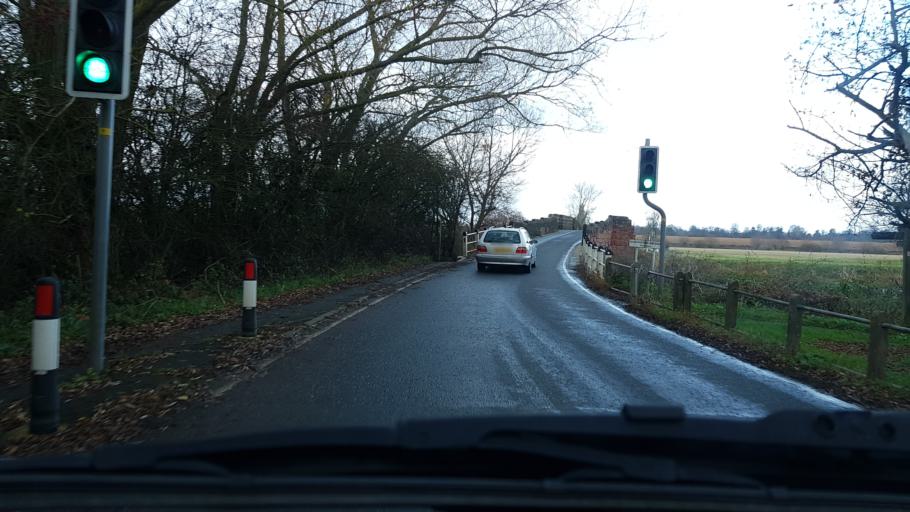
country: GB
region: England
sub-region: Worcestershire
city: Bredon
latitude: 52.0788
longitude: -2.1152
